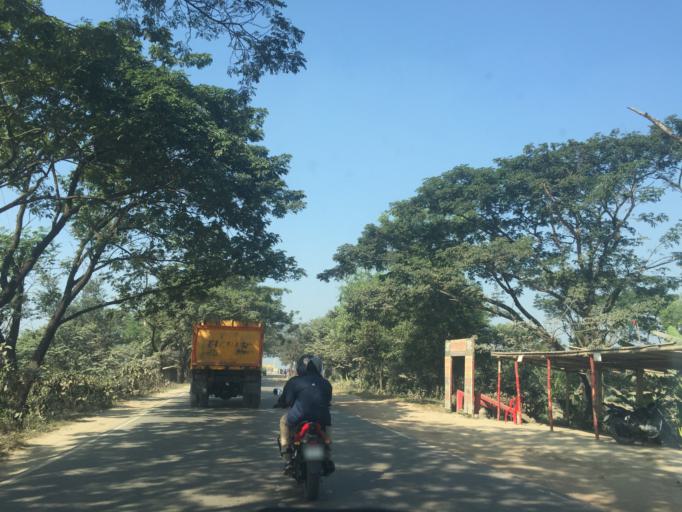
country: BD
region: Dhaka
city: Tungi
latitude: 23.8300
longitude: 90.3424
